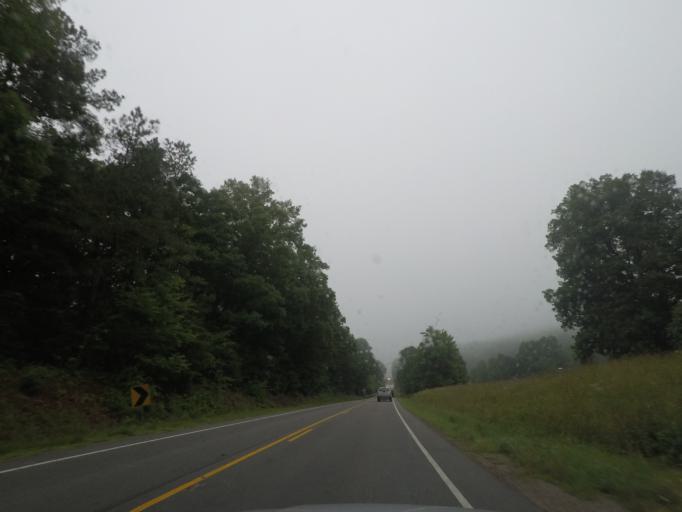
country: US
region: Virginia
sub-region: Buckingham County
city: Buckingham
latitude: 37.4658
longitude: -78.4700
